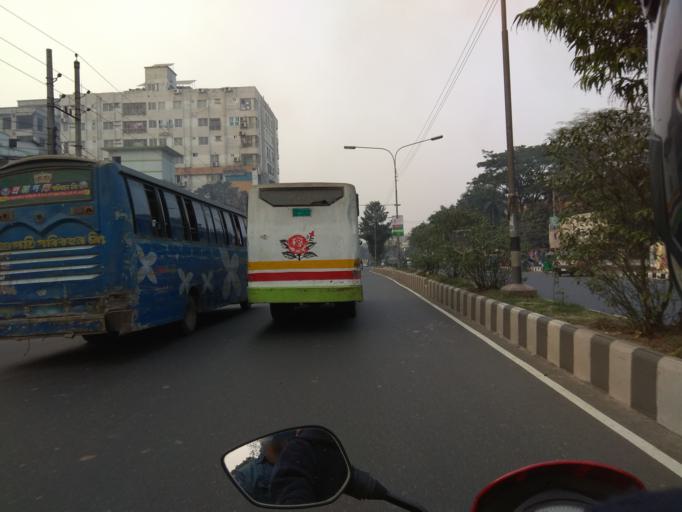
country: BD
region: Dhaka
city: Azimpur
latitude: 23.7703
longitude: 90.3683
